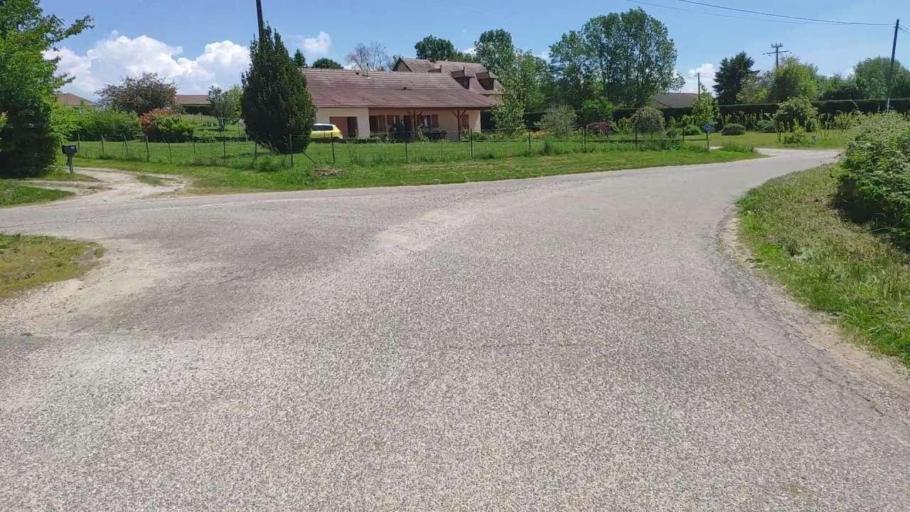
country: FR
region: Franche-Comte
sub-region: Departement du Jura
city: Bletterans
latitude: 46.7435
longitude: 5.4059
